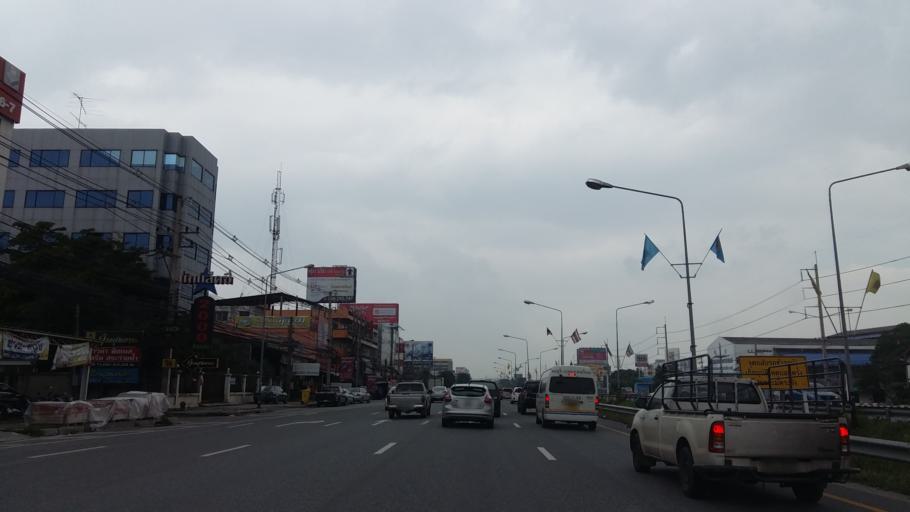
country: TH
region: Chon Buri
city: Chon Buri
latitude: 13.3269
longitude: 100.9651
